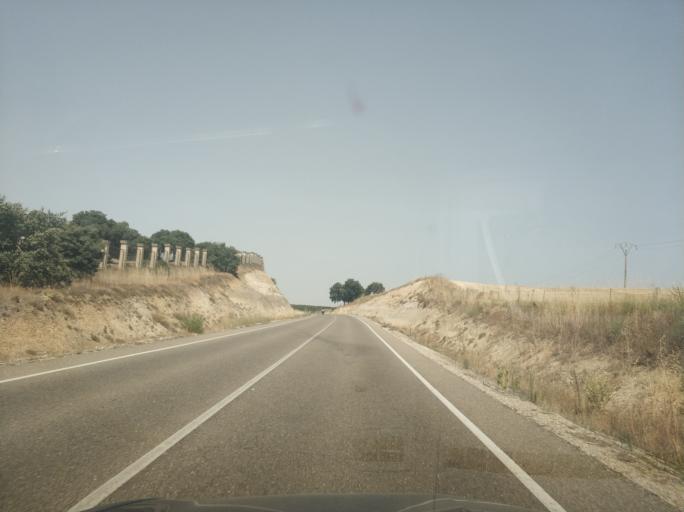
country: ES
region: Castille and Leon
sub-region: Provincia de Salamanca
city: Florida de Liebana
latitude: 41.0347
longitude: -5.7343
